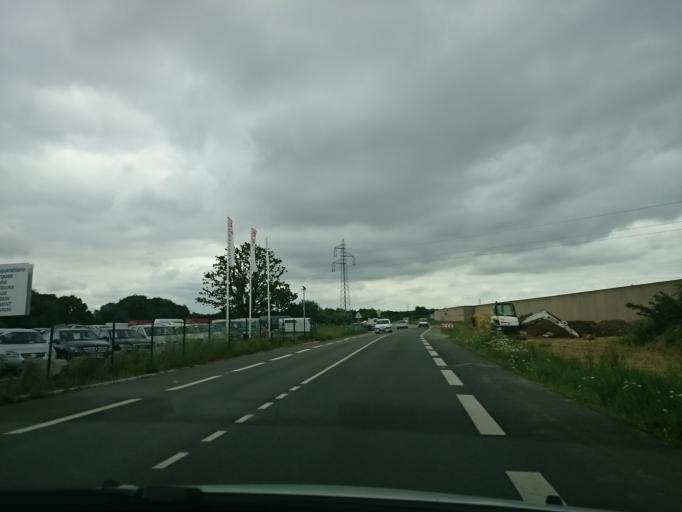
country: FR
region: Pays de la Loire
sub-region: Departement de la Loire-Atlantique
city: La Montagne
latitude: 47.1757
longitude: -1.6934
